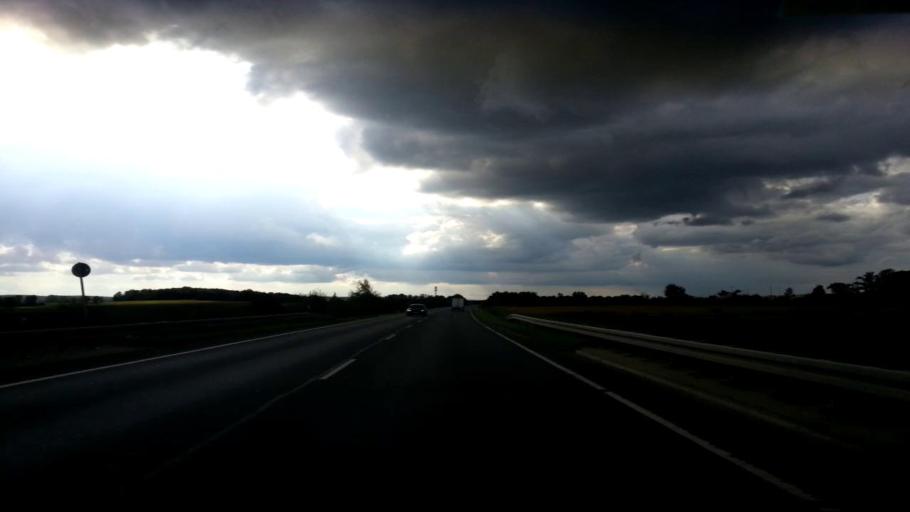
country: DE
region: Bavaria
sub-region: Regierungsbezirk Mittelfranken
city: Adelsdorf
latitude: 49.6999
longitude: 10.8680
